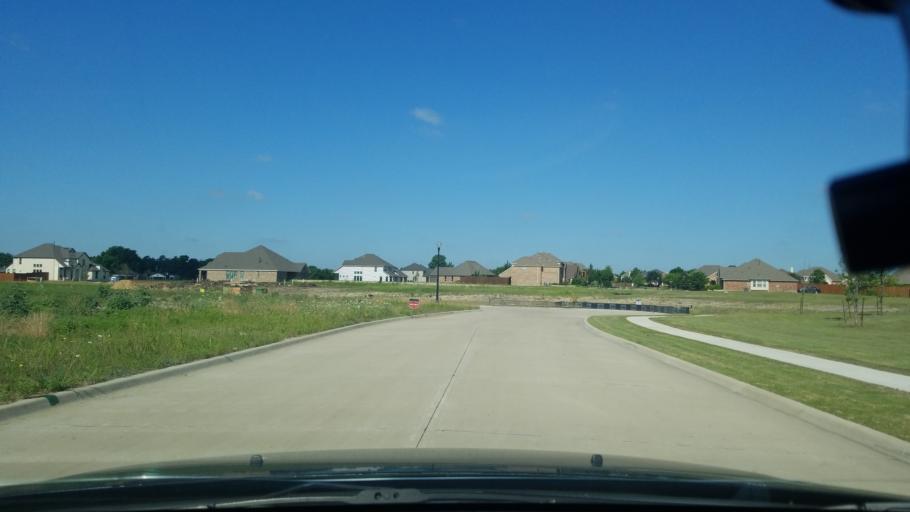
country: US
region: Texas
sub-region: Dallas County
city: Sunnyvale
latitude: 32.8041
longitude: -96.5804
